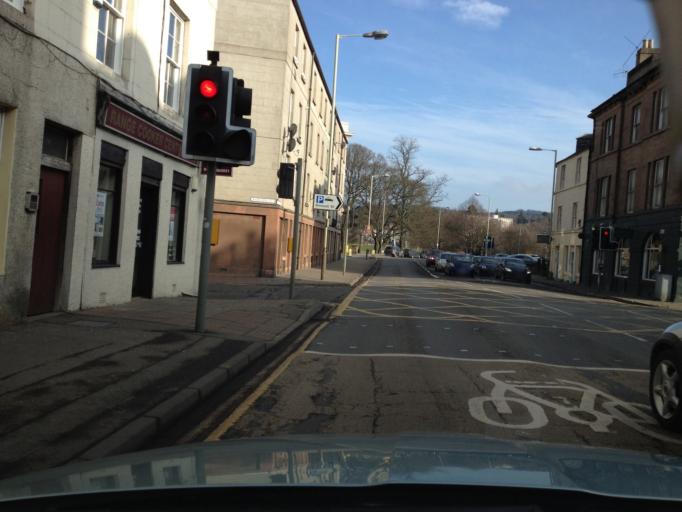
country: GB
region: Scotland
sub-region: Perth and Kinross
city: Perth
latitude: 56.3995
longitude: -3.4332
